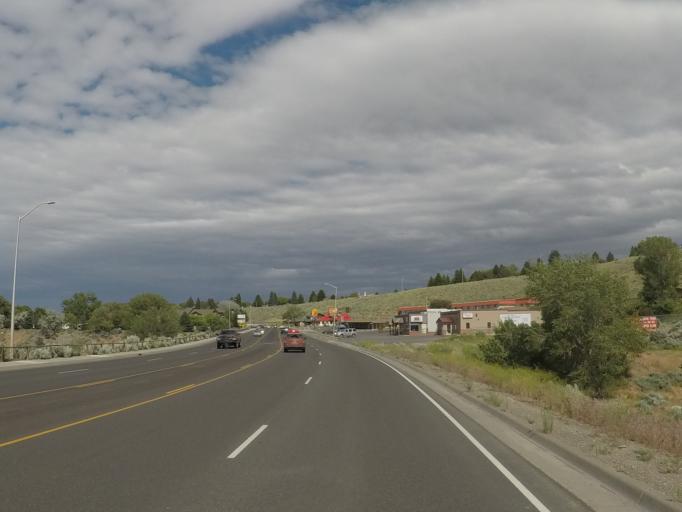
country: US
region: Wyoming
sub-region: Park County
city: Cody
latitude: 44.5166
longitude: -109.0772
